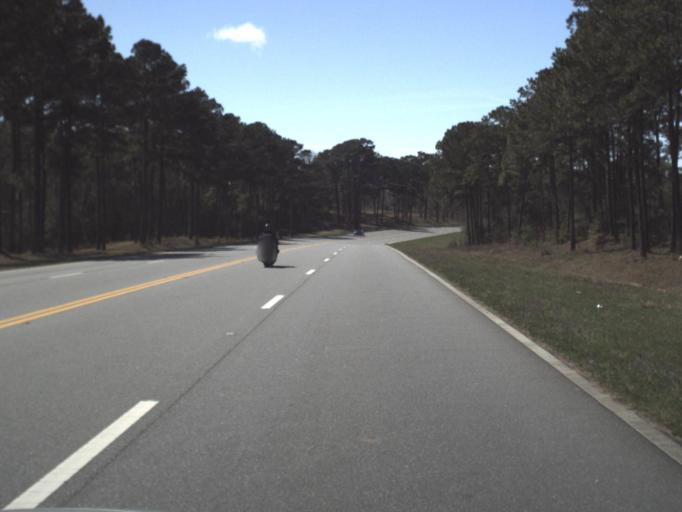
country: US
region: Florida
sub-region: Gadsden County
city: Chattahoochee
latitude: 30.7006
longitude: -84.8069
